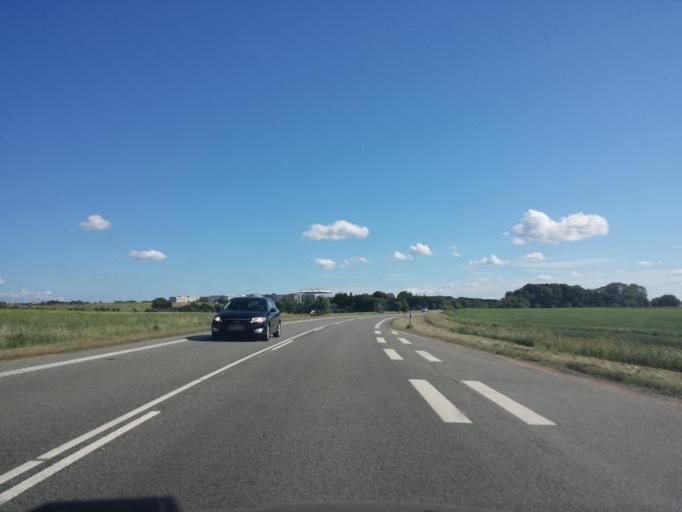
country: DK
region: Capital Region
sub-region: Egedal Kommune
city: Smorumnedre
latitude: 55.7668
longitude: 12.2944
